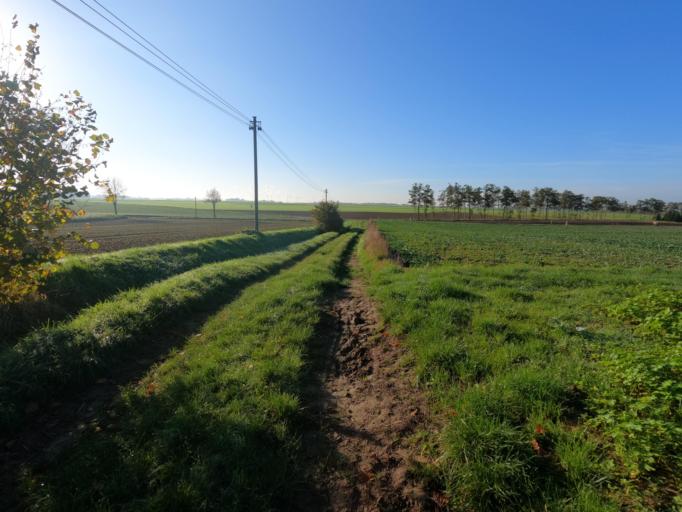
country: DE
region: North Rhine-Westphalia
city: Erkelenz
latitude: 51.0805
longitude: 6.3816
